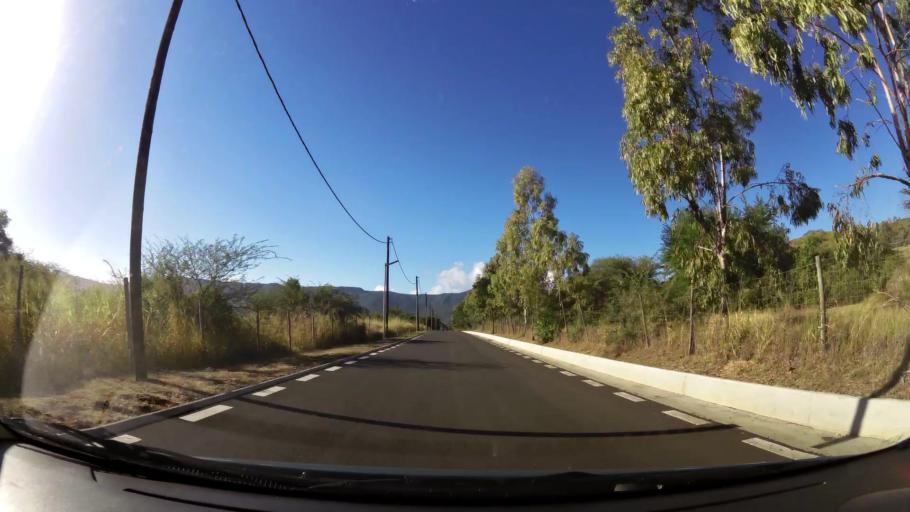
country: MU
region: Black River
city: Tamarin
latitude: -20.3396
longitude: 57.3861
